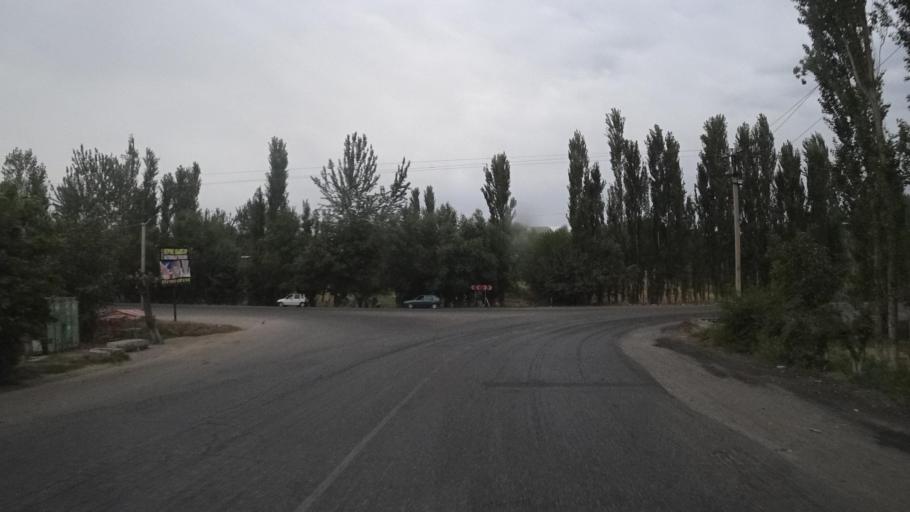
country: UZ
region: Namangan
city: Haqqulobod Shahri
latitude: 41.0498
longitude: 72.3106
